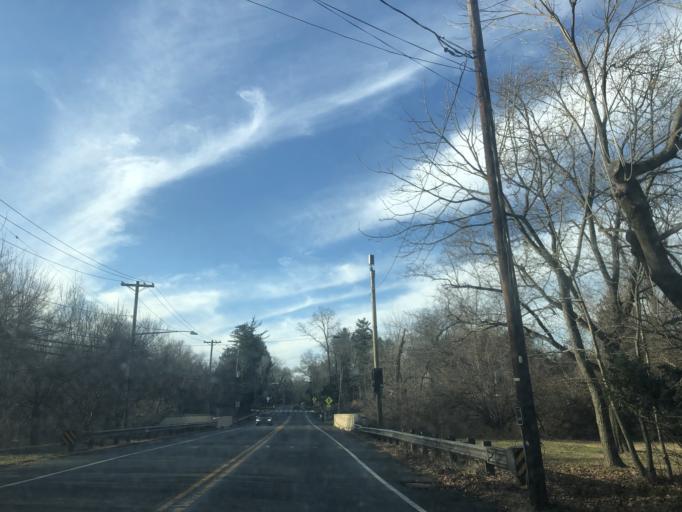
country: US
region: New Jersey
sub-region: Somerset County
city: Kingston
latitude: 40.3665
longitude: -74.6267
